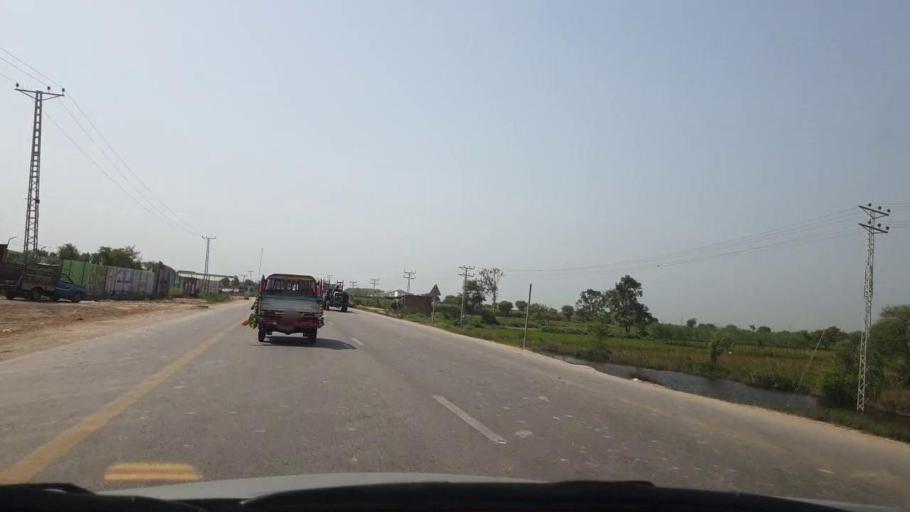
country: PK
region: Sindh
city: Matli
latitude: 25.0260
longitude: 68.6530
